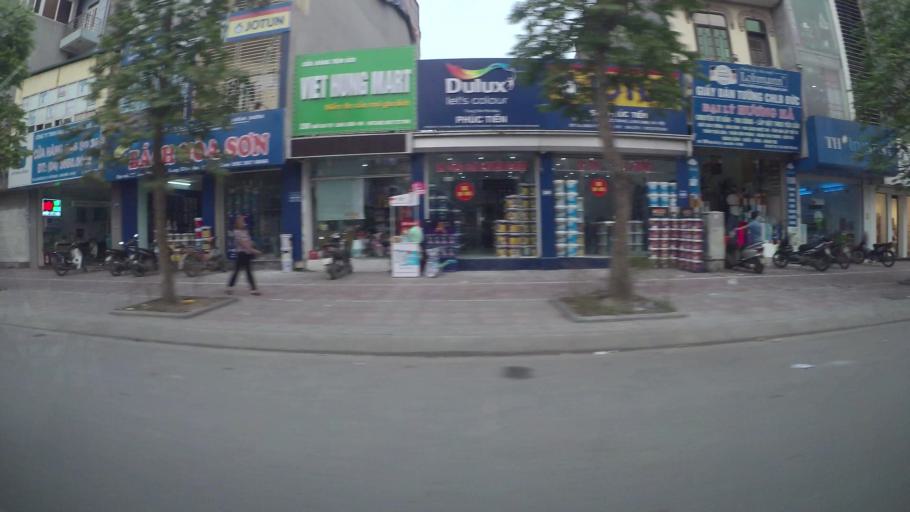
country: VN
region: Ha Noi
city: Hoan Kiem
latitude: 21.0618
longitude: 105.8947
